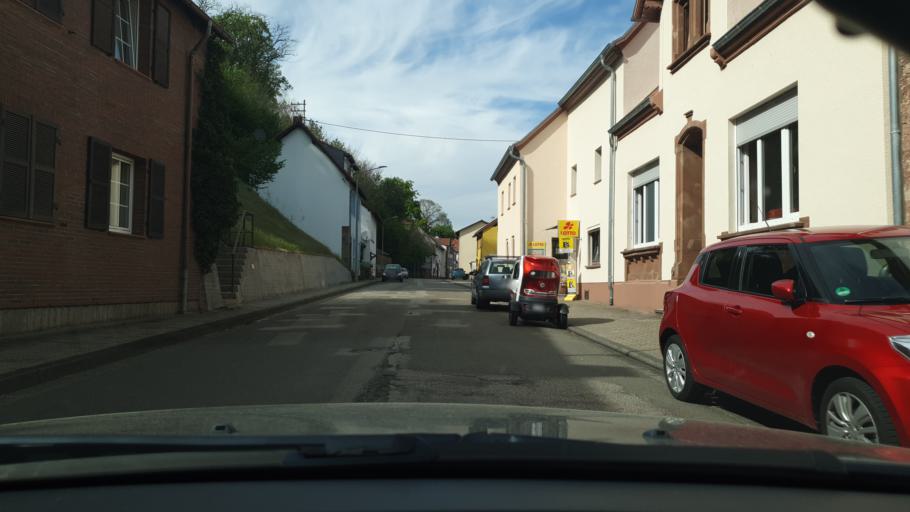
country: DE
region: Rheinland-Pfalz
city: Wallhalben
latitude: 49.3168
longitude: 7.5215
